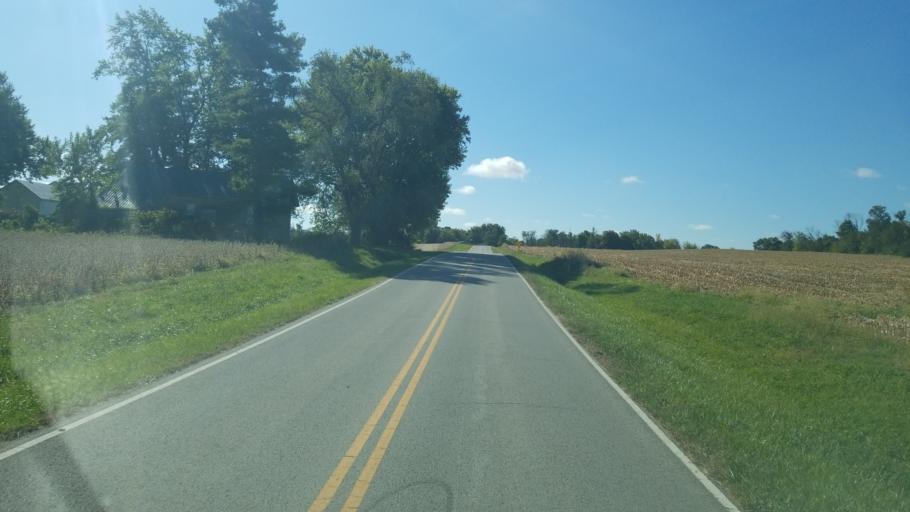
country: US
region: Ohio
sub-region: Highland County
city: Leesburg
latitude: 39.2913
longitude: -83.5799
